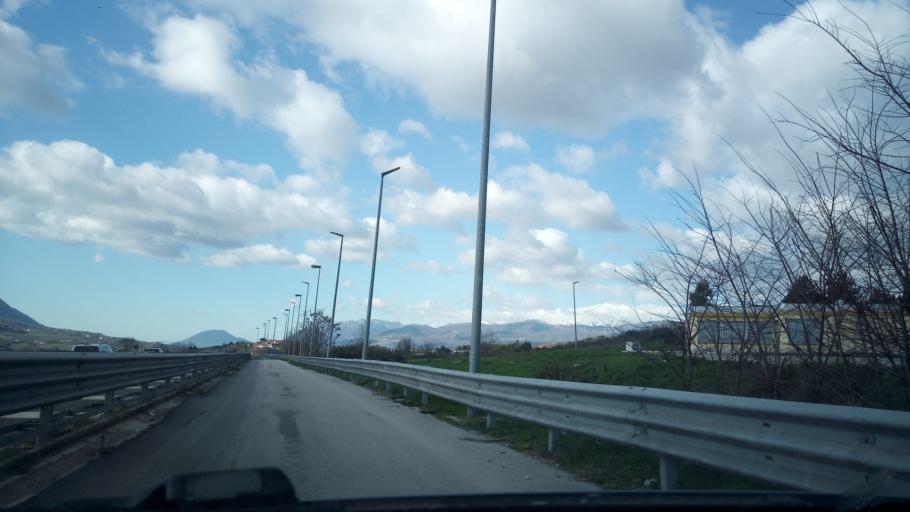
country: IT
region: Campania
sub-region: Provincia di Benevento
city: Ponte
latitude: 41.1869
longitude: 14.7464
